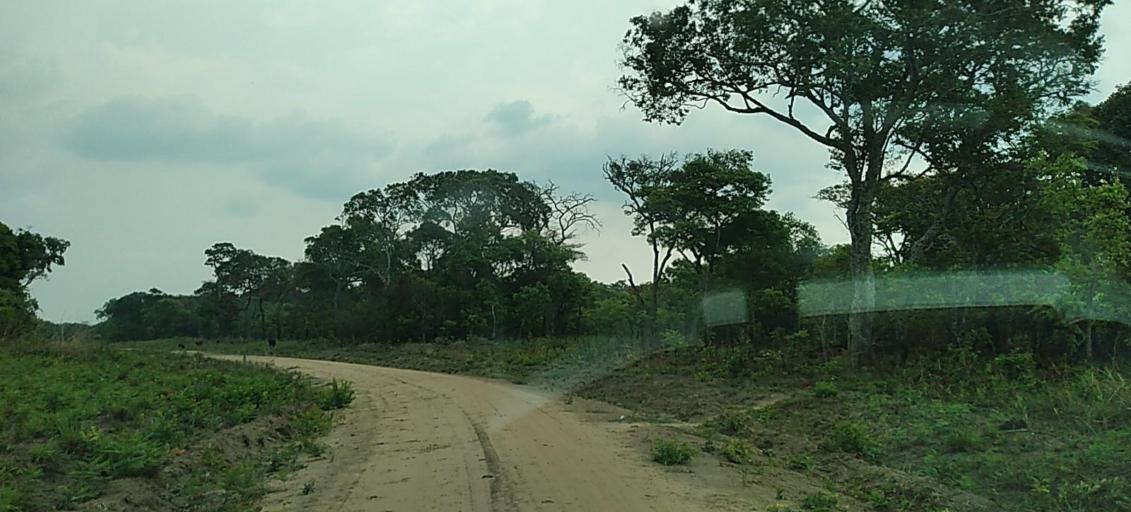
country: ZM
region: North-Western
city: Mwinilunga
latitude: -11.4080
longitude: 24.6209
